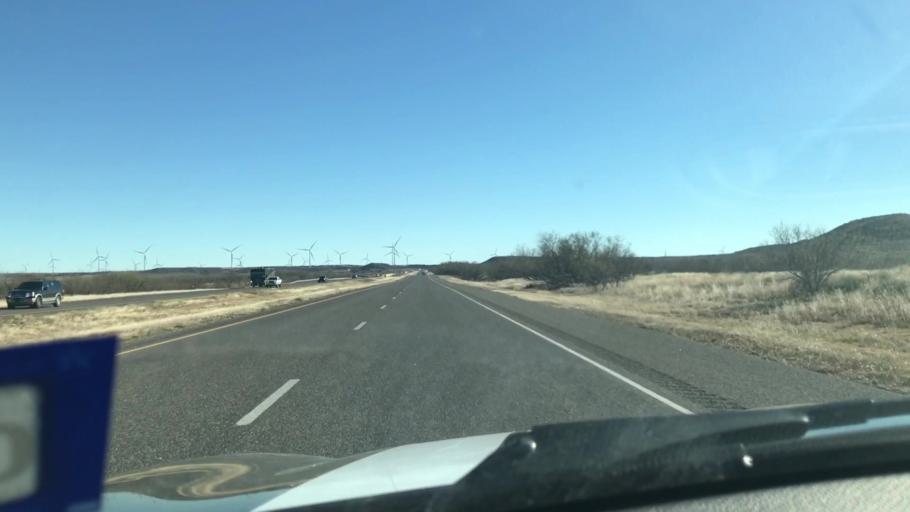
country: US
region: Texas
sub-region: Scurry County
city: Snyder
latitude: 32.9338
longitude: -101.0716
